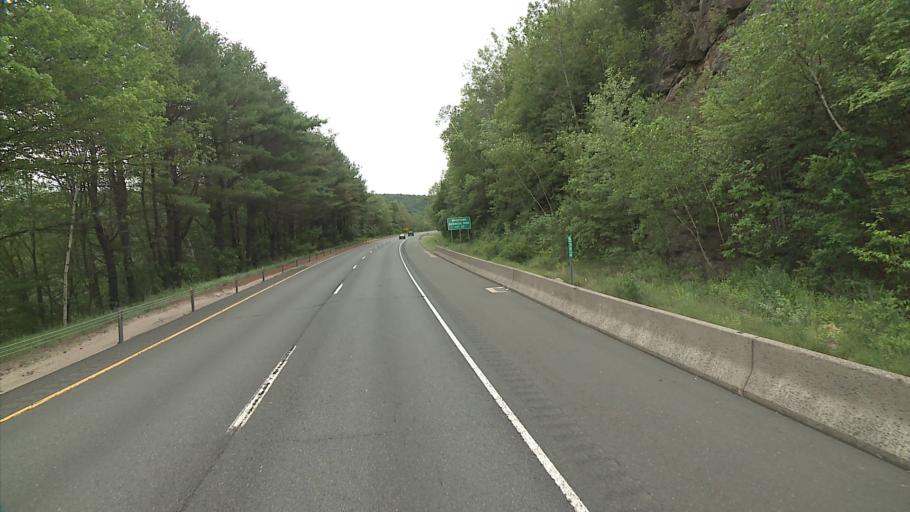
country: US
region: Connecticut
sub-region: Litchfield County
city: Oakville
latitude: 41.6205
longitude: -73.0650
